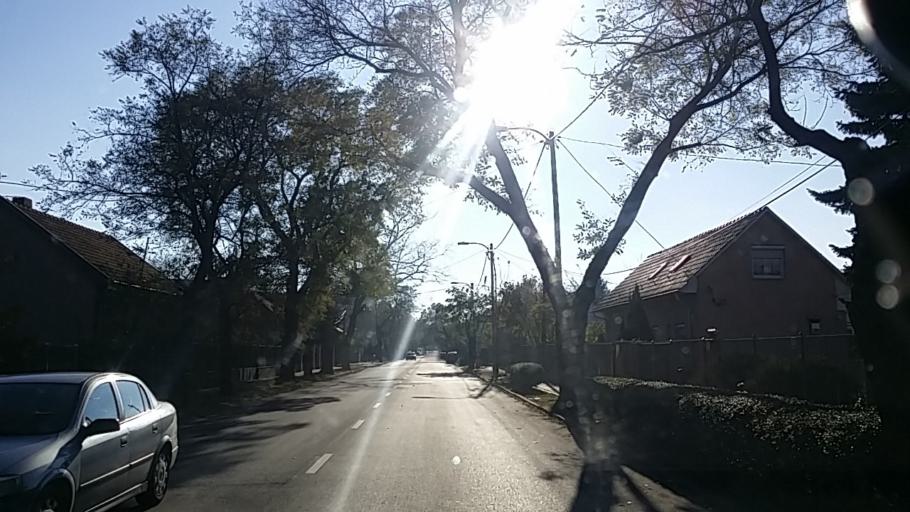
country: HU
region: Budapest
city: Budapest XVIII. keruelet
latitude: 47.4441
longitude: 19.1896
